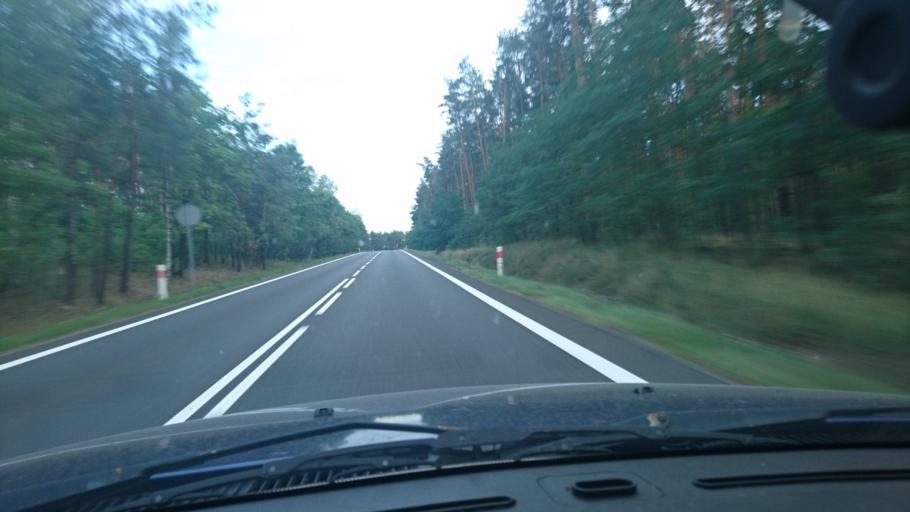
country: PL
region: Silesian Voivodeship
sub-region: Powiat lubliniecki
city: Lubliniec
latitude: 50.6012
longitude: 18.7013
